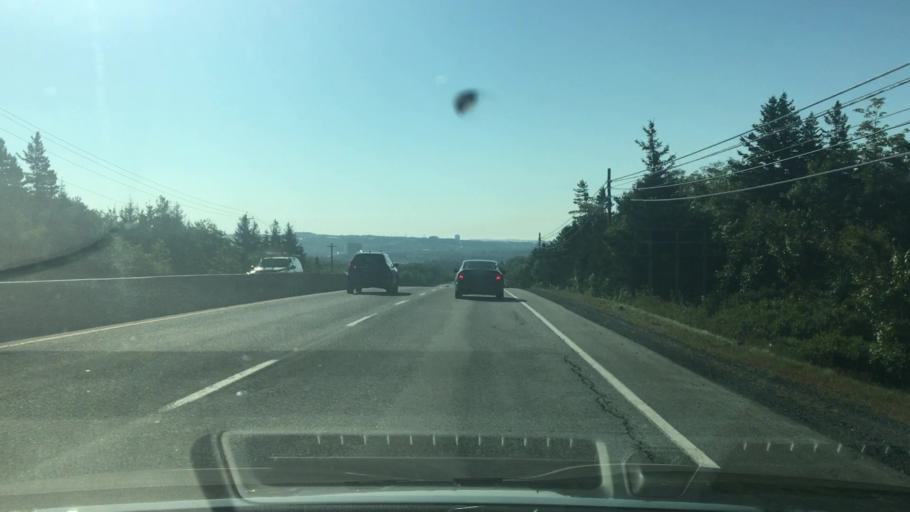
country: CA
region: Nova Scotia
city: Dartmouth
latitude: 44.7164
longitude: -63.6333
